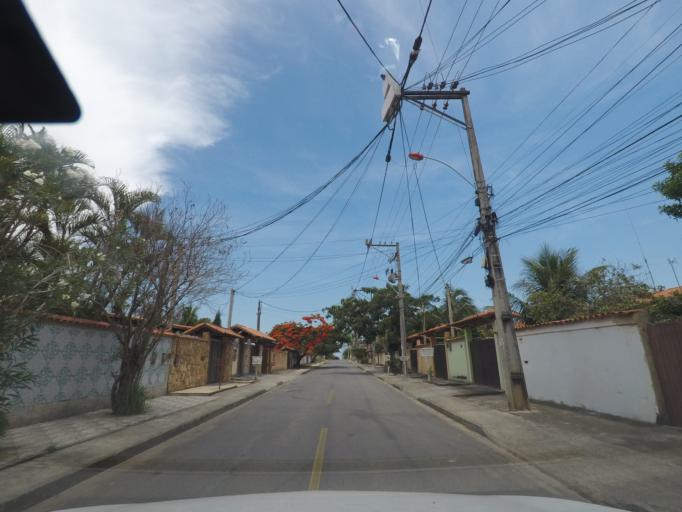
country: BR
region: Rio de Janeiro
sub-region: Niteroi
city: Niteroi
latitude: -22.9636
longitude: -42.9756
